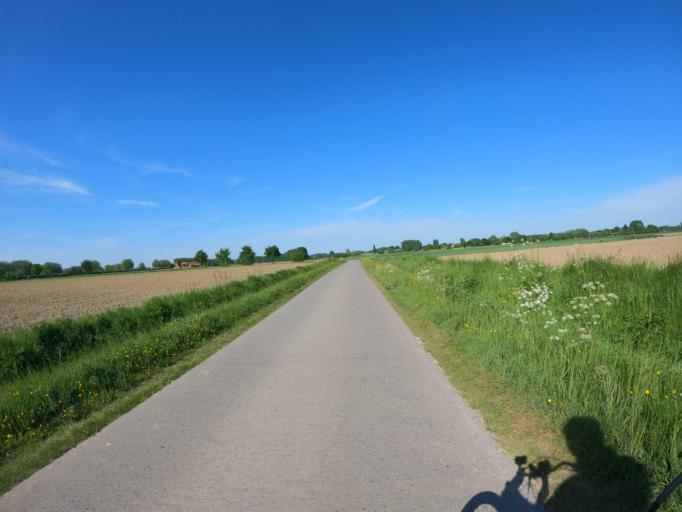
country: BE
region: Flanders
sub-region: Provincie Oost-Vlaanderen
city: Oosterzele
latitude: 50.9185
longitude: 3.7747
